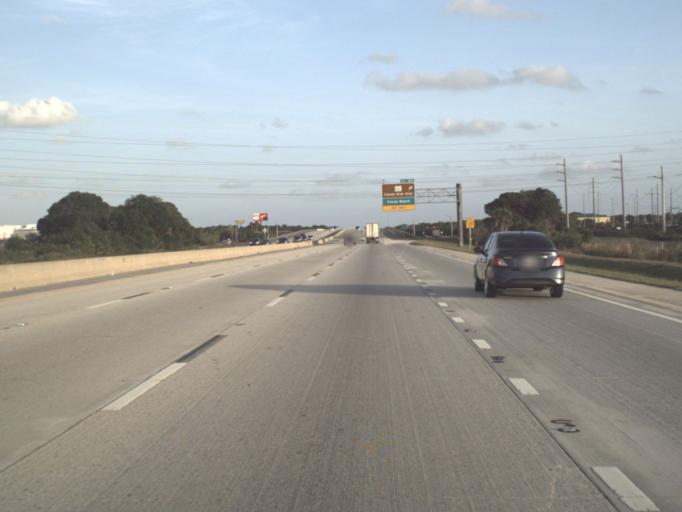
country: US
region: Florida
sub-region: Brevard County
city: Cocoa West
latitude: 28.3646
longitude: -80.7979
